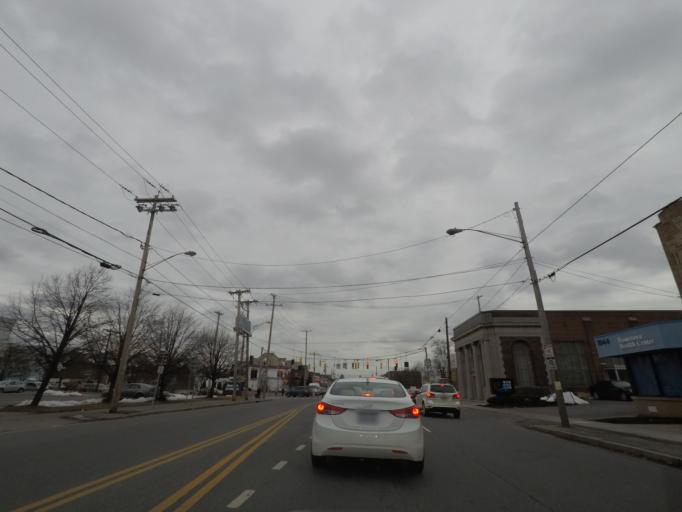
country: US
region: New York
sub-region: Schenectady County
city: Schenectady
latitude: 42.8014
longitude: -73.9278
